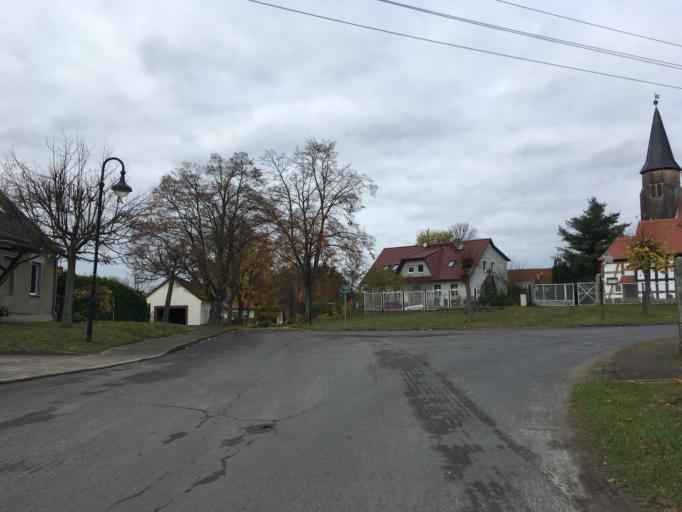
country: DE
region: Brandenburg
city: Jamlitz
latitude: 52.0893
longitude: 14.4327
